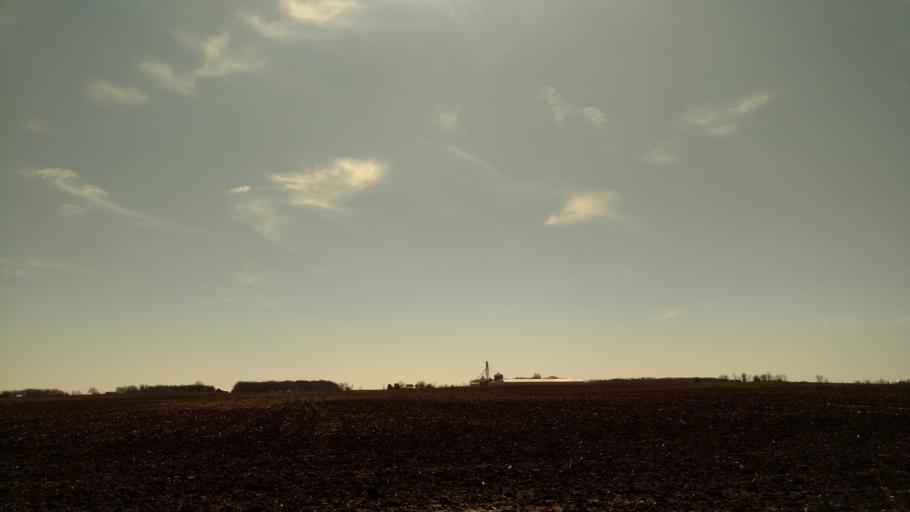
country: US
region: Ohio
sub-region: Union County
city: Richwood
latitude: 40.5284
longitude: -83.2740
